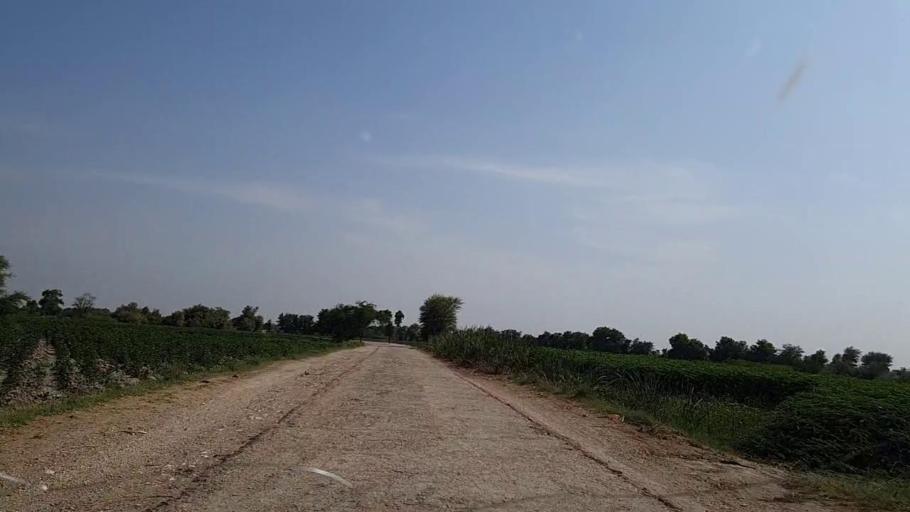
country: PK
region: Sindh
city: Khanpur
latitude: 27.7415
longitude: 69.3418
